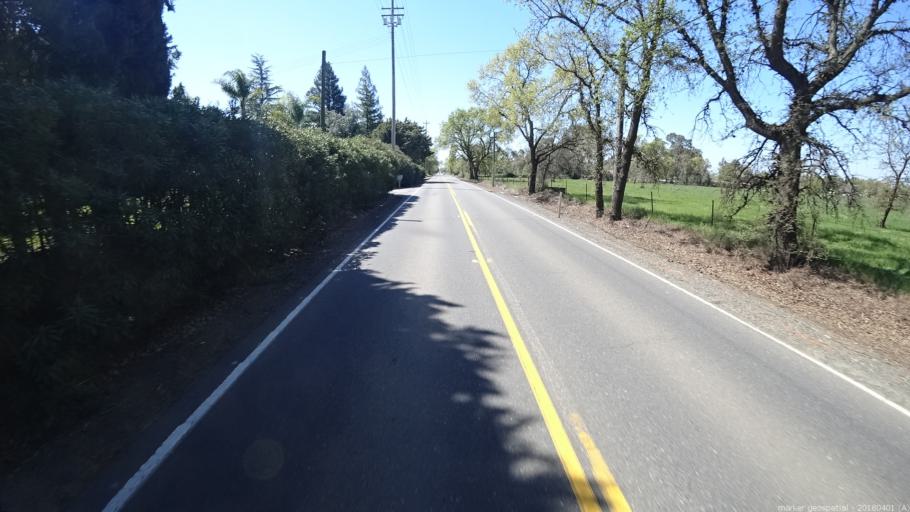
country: US
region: California
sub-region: Sacramento County
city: Wilton
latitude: 38.4407
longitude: -121.1913
